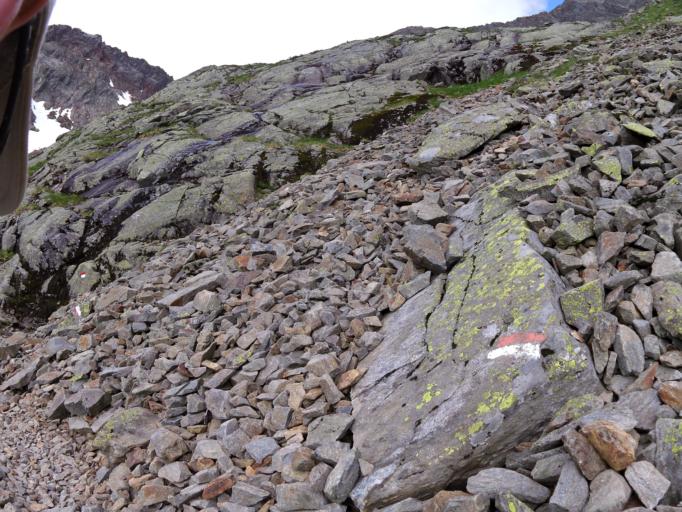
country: AT
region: Tyrol
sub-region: Politischer Bezirk Innsbruck Land
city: Gschnitz
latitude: 47.0402
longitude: 11.3032
